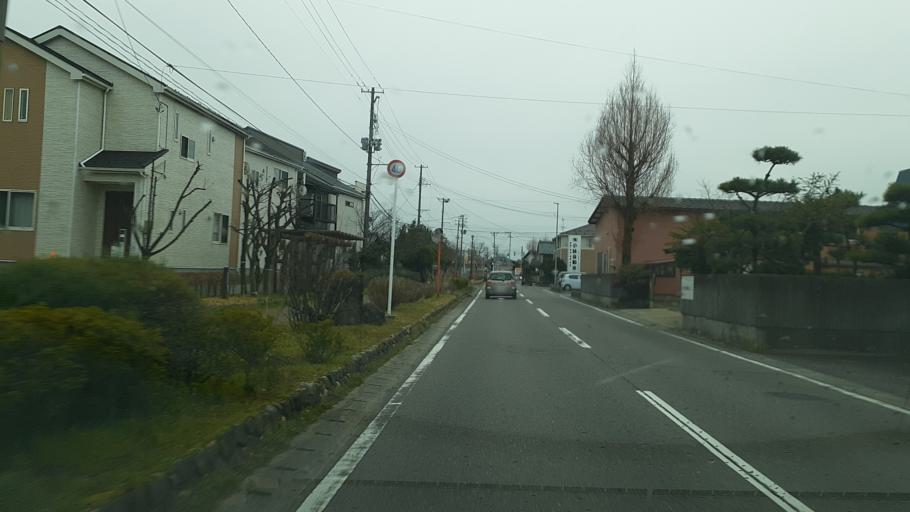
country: JP
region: Niigata
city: Niigata-shi
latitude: 37.8601
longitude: 139.0357
